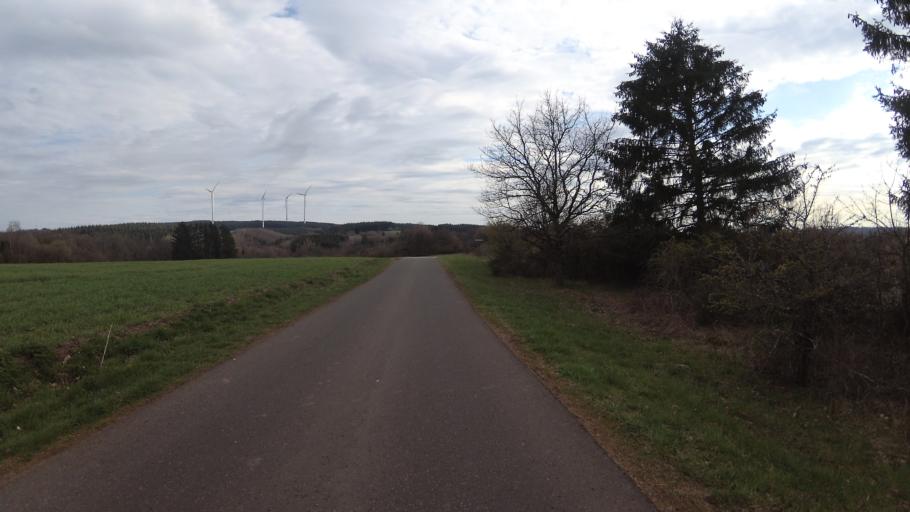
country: DE
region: Rheinland-Pfalz
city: Hahnweiler
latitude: 49.5611
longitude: 7.2137
